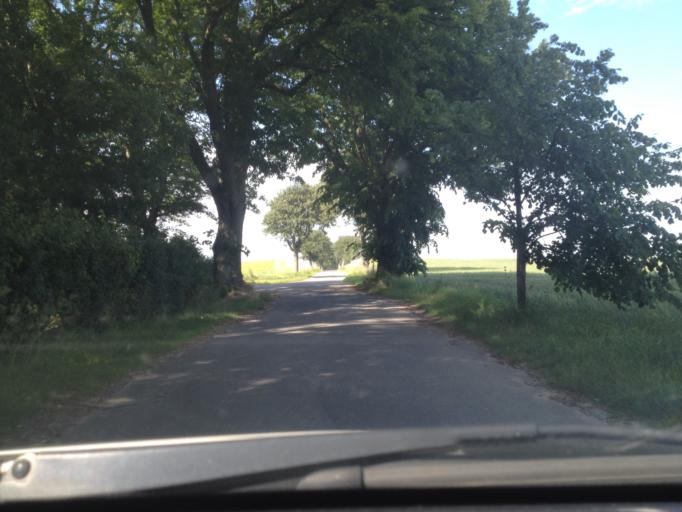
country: DK
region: Central Jutland
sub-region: Samso Kommune
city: Tranebjerg
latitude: 55.7843
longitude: 10.5878
